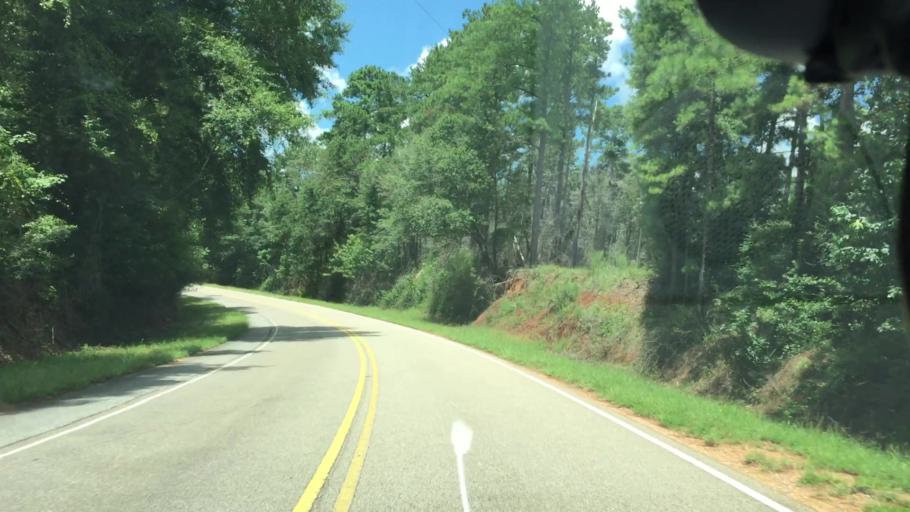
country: US
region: Alabama
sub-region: Coffee County
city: New Brockton
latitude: 31.4081
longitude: -85.8426
